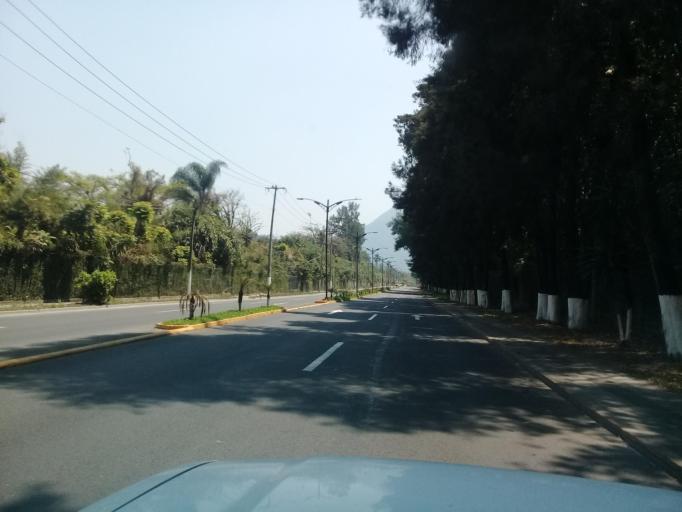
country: MX
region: Veracruz
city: Ixtac Zoquitlan
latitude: 18.8621
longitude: -97.0462
